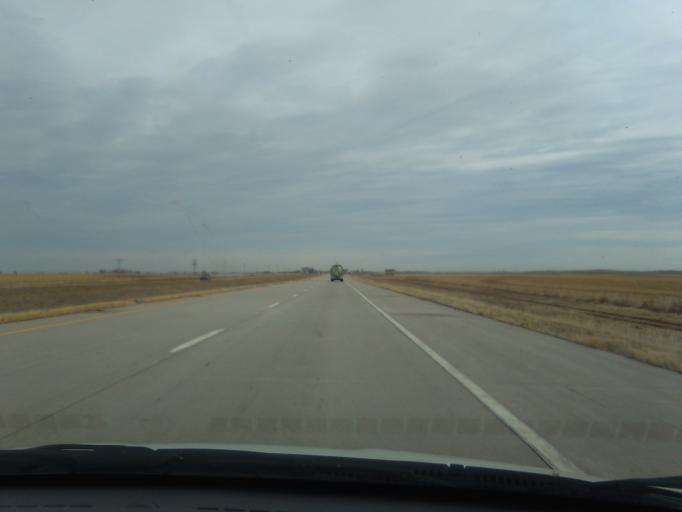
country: US
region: Colorado
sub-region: Morgan County
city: Fort Morgan
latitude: 40.2321
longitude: -104.1283
